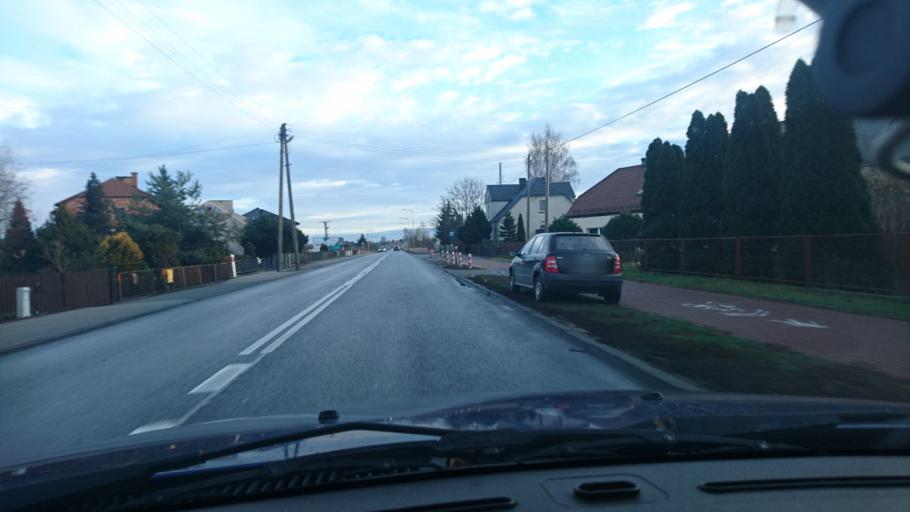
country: PL
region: Greater Poland Voivodeship
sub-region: Powiat kepinski
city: Kepno
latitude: 51.2721
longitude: 17.9925
